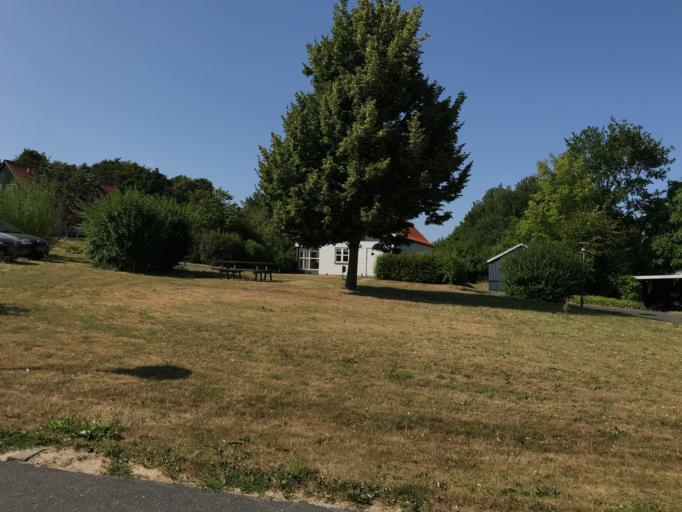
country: DK
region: North Denmark
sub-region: Alborg Kommune
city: Gistrup
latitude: 56.9311
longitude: 10.0408
